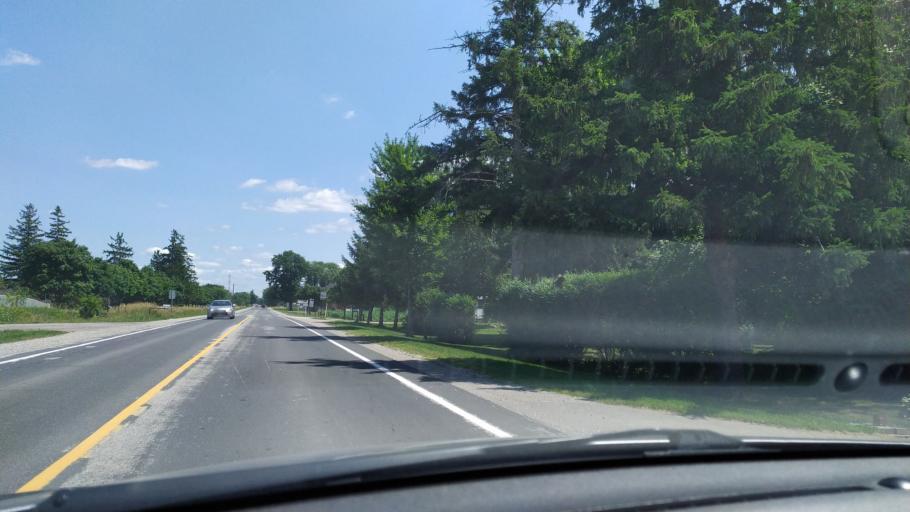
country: CA
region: Ontario
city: Stratford
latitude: 43.3525
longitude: -80.9540
